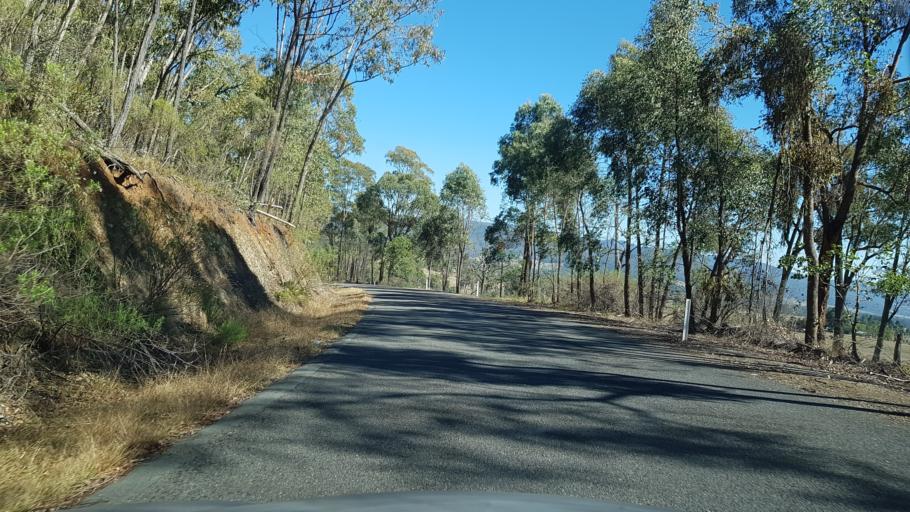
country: AU
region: Victoria
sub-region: Mansfield
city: Mansfield
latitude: -36.8144
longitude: 146.4603
